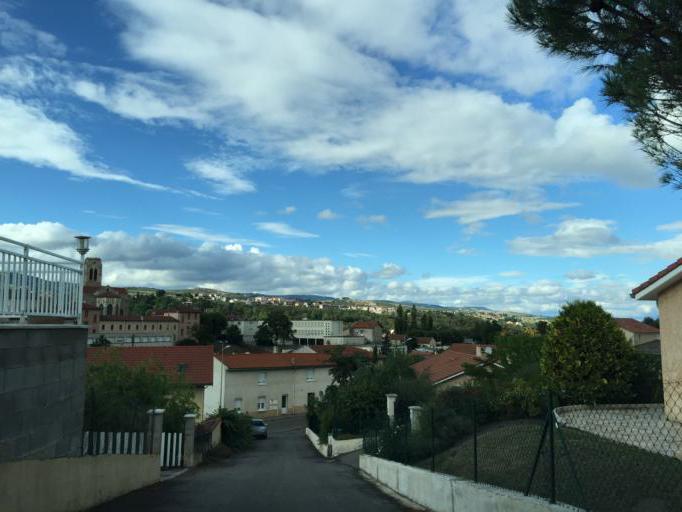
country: FR
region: Rhone-Alpes
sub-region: Departement de la Loire
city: La Grand-Croix
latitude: 45.4833
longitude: 4.5458
